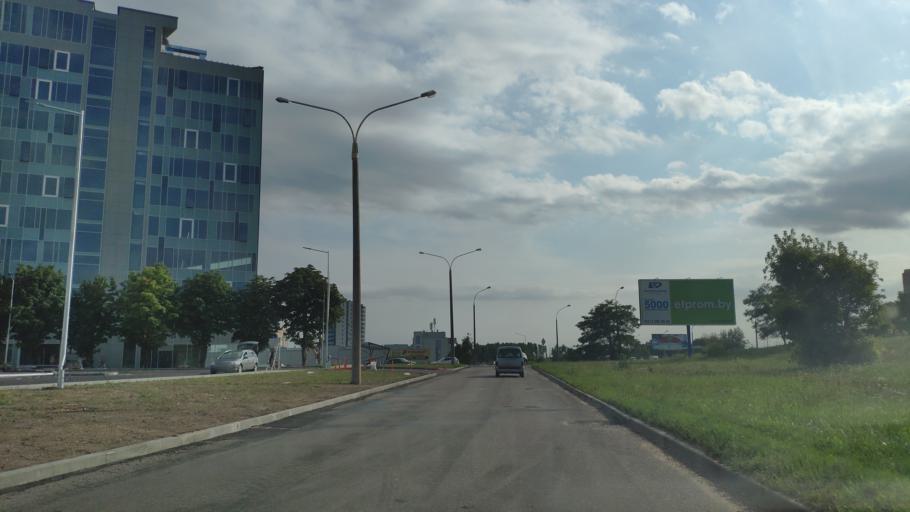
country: BY
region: Minsk
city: Vyaliki Trastsyanets
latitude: 53.8650
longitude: 27.6881
